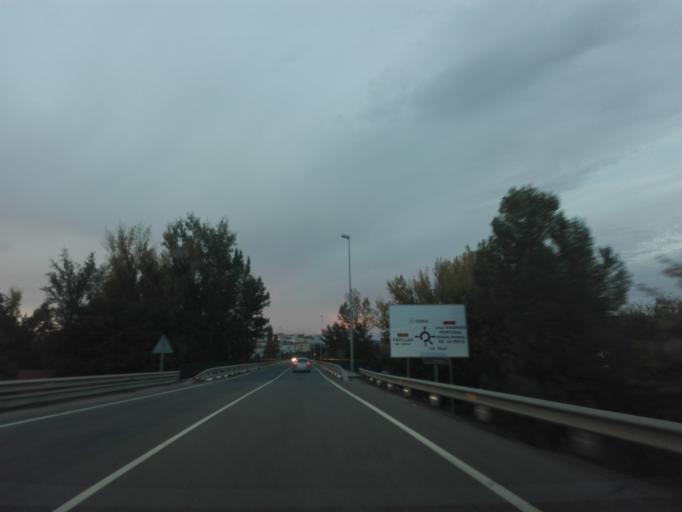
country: ES
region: Extremadura
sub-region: Provincia de Caceres
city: Coria
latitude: 39.9773
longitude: -6.5275
